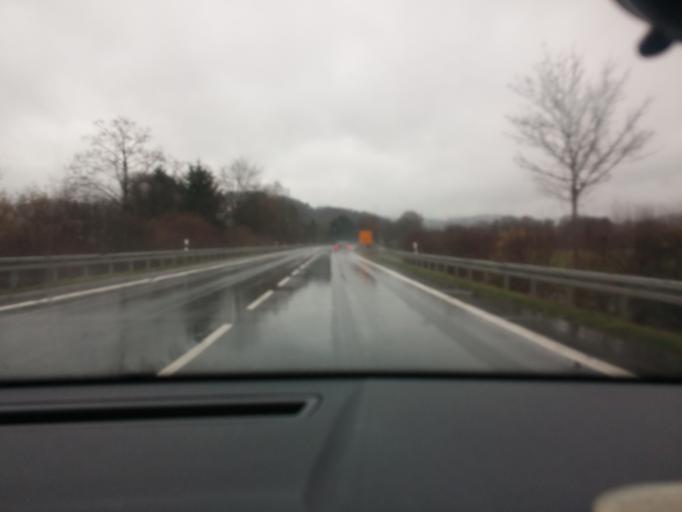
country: DE
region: Hesse
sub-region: Regierungsbezirk Darmstadt
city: Brensbach
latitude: 49.7709
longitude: 8.8769
